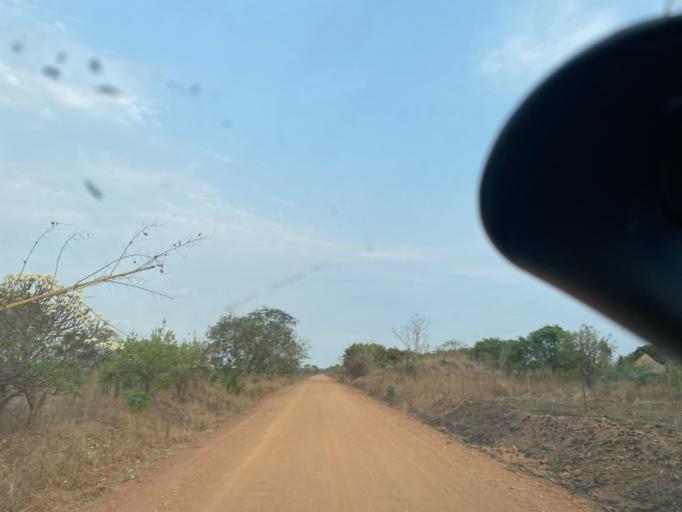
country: ZM
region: Lusaka
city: Chongwe
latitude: -15.2208
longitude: 28.5836
